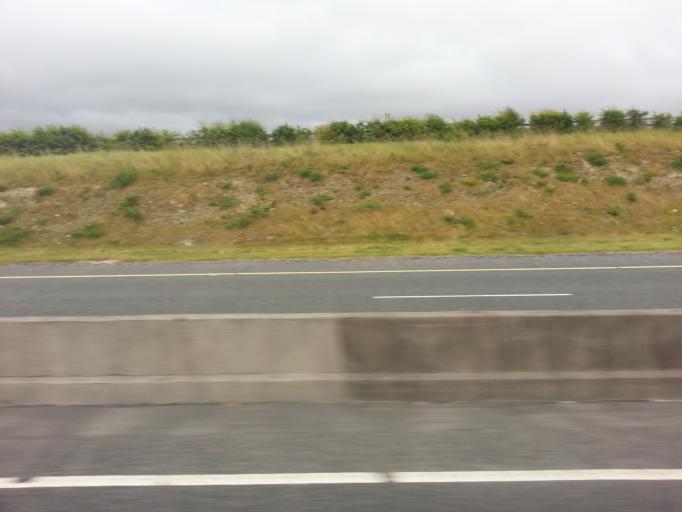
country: IE
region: Leinster
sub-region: County Carlow
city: Carlow
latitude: 52.8266
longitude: -6.8490
